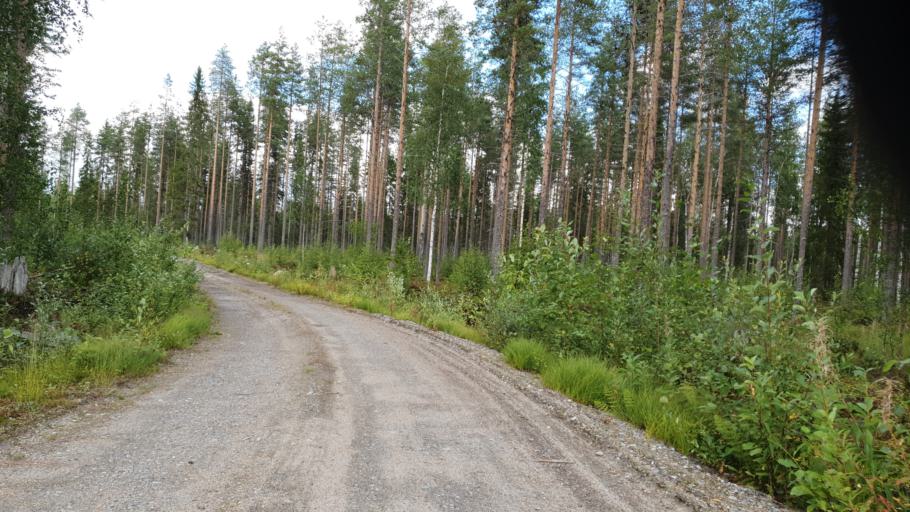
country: FI
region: Kainuu
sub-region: Kehys-Kainuu
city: Kuhmo
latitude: 64.1429
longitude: 29.3875
